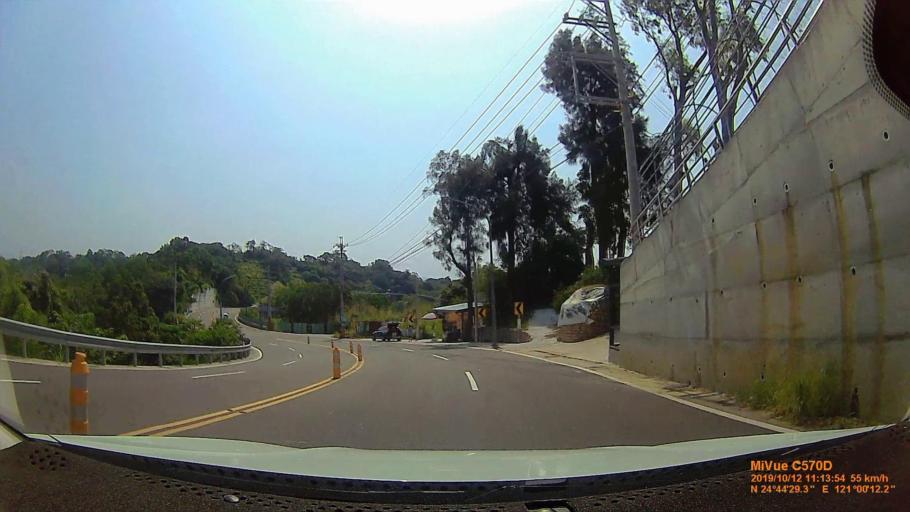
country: TW
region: Taiwan
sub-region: Hsinchu
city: Hsinchu
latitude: 24.7413
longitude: 121.0034
